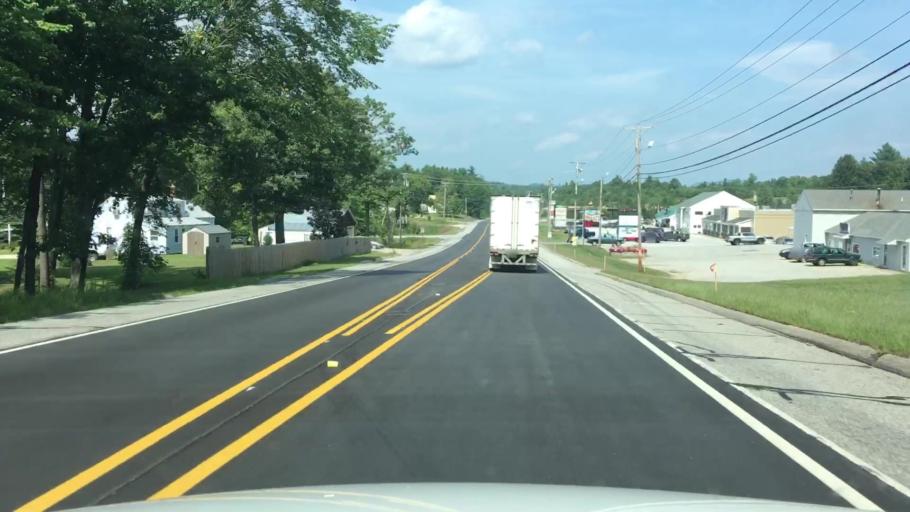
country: US
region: Maine
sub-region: Androscoggin County
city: Turner
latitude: 44.2675
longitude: -70.2673
